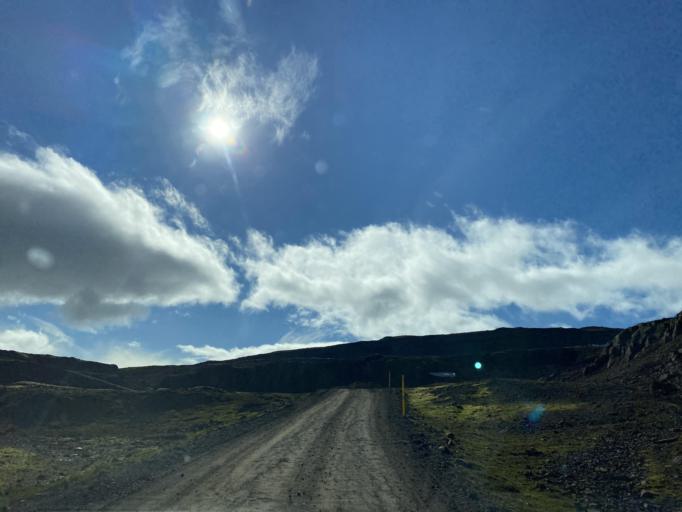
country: IS
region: East
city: Eskifjoerdur
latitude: 65.1697
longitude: -14.1230
